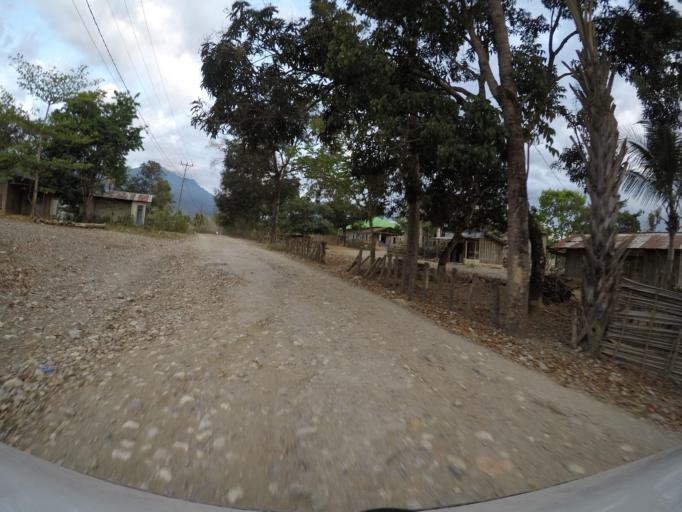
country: TL
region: Bobonaro
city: Maliana
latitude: -8.9151
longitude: 125.2146
